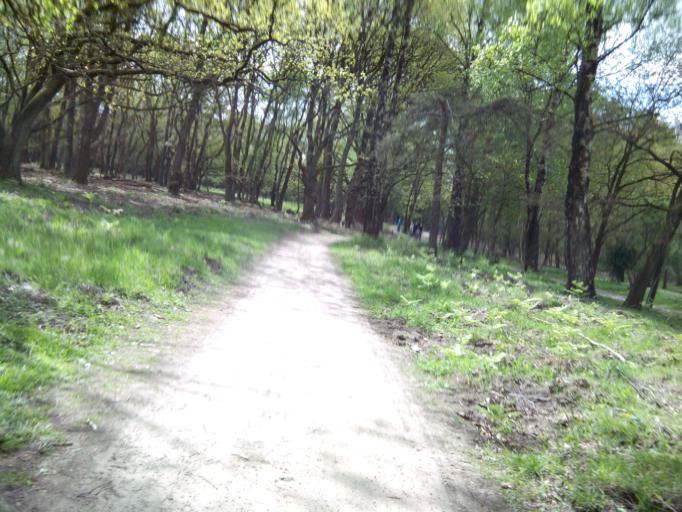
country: NL
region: Gelderland
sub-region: Gemeente Renkum
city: Wolfheze
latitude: 52.0457
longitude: 5.7758
